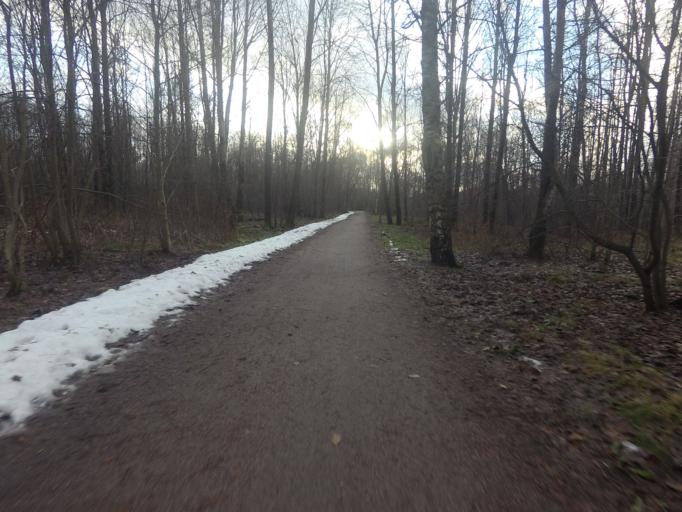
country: FI
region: Uusimaa
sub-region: Helsinki
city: Koukkuniemi
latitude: 60.1865
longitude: 24.7655
